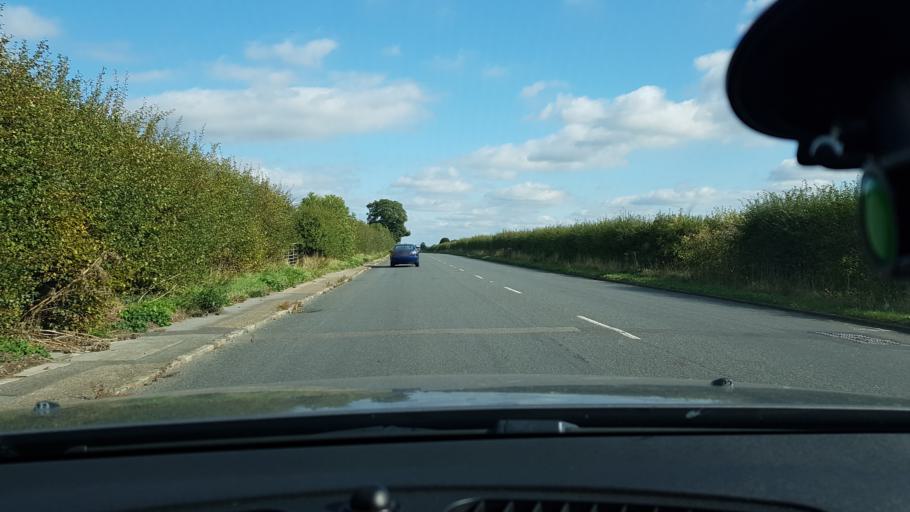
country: GB
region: England
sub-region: West Berkshire
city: Kintbury
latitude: 51.4143
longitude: -1.4744
